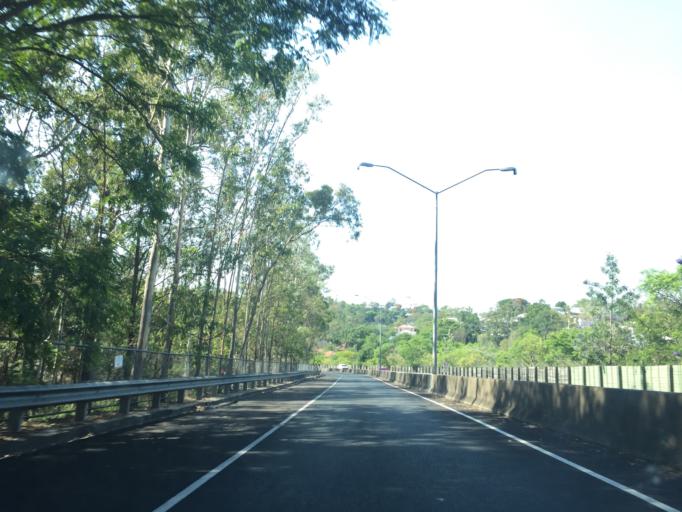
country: AU
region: Queensland
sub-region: Brisbane
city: Milton
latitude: -27.4619
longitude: 152.9883
